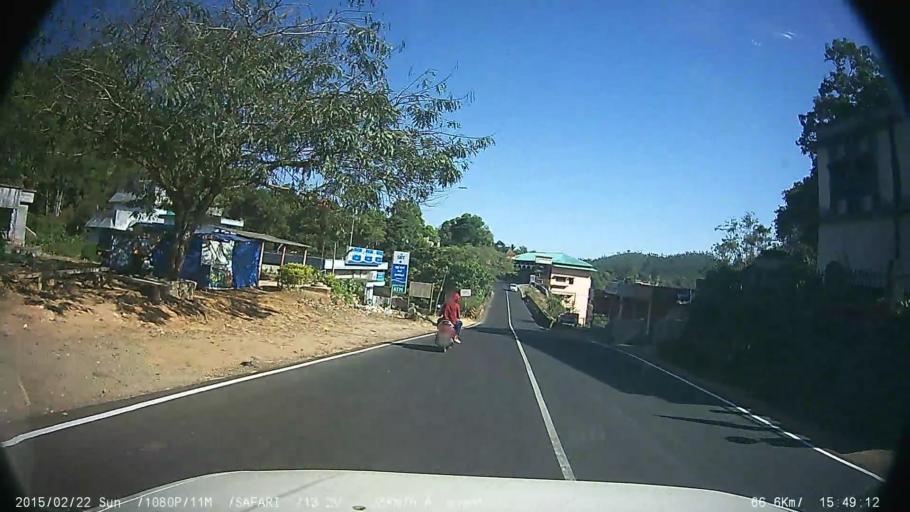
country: IN
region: Kerala
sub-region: Kottayam
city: Erattupetta
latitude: 9.5716
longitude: 76.9961
